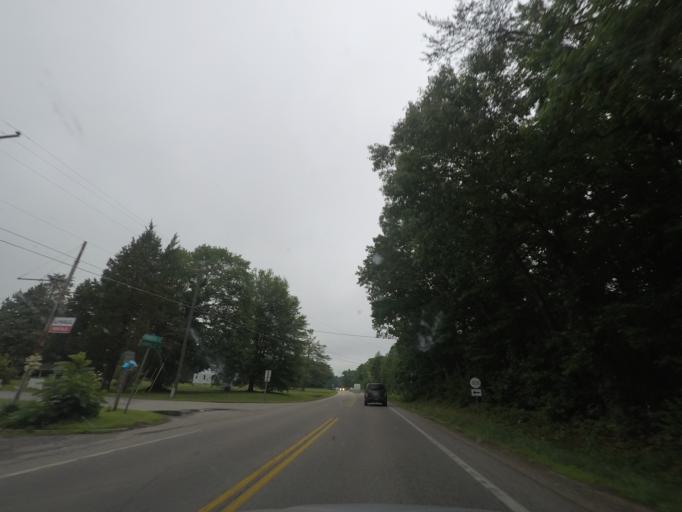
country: US
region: Virginia
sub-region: Prince Edward County
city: Hampden Sydney
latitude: 37.2527
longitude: -78.4231
